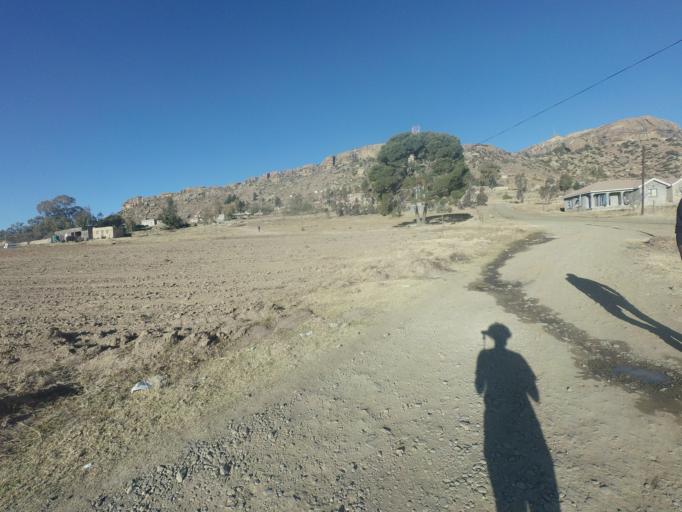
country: LS
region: Maseru
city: Maseru
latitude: -29.3024
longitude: 27.5488
